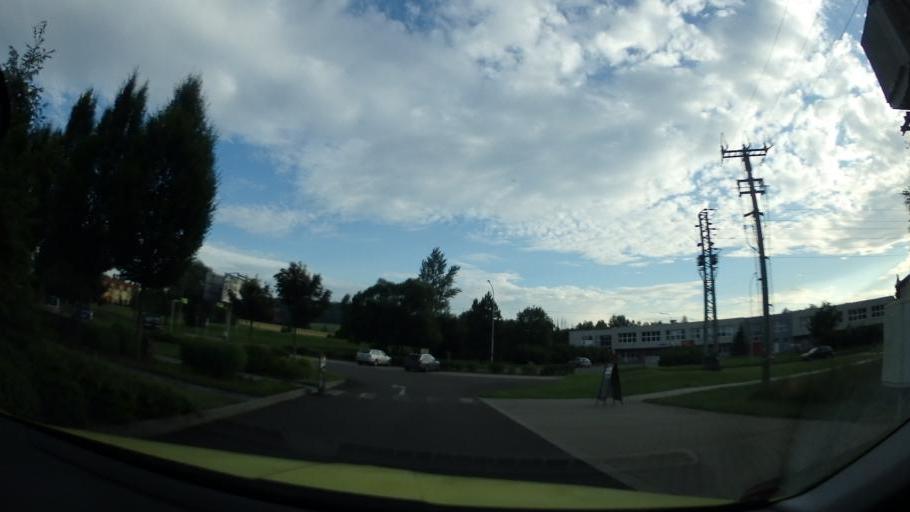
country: CZ
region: Moravskoslezsky
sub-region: Okres Novy Jicin
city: Novy Jicin
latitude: 49.5900
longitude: 17.9990
